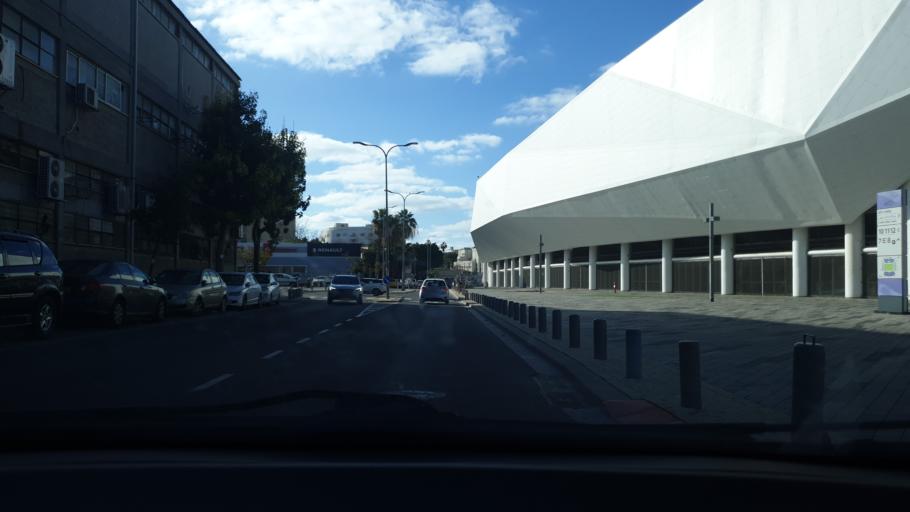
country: IL
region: Tel Aviv
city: Yafo
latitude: 32.0506
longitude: 34.7622
